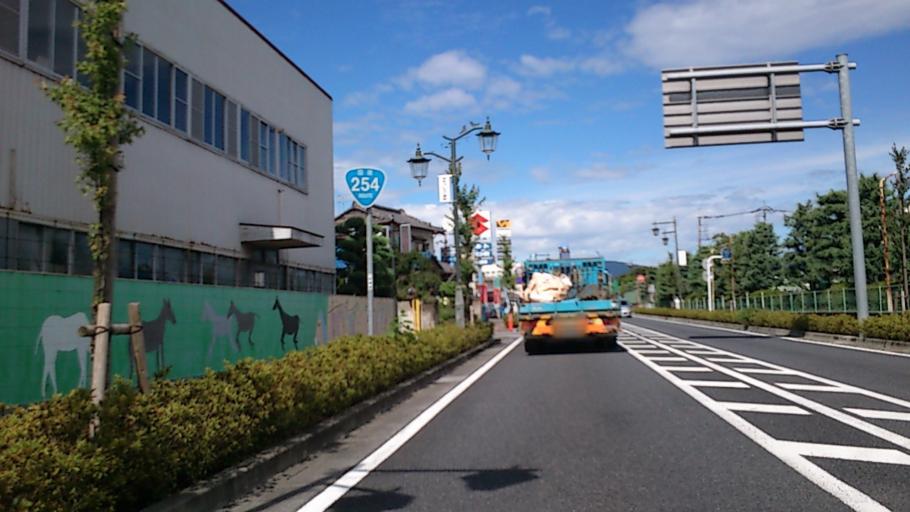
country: JP
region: Gunma
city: Tomioka
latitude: 36.2584
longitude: 138.9043
